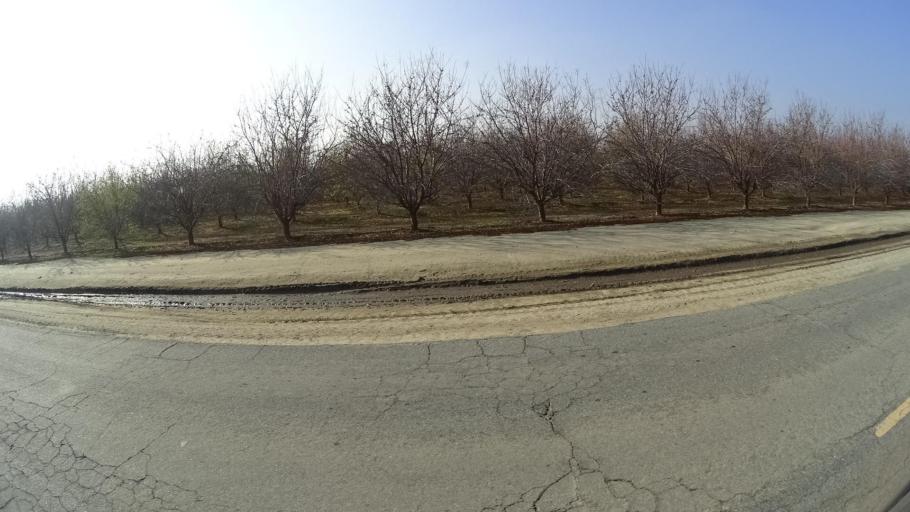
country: US
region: California
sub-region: Kern County
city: Greenfield
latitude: 35.2321
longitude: -119.0391
